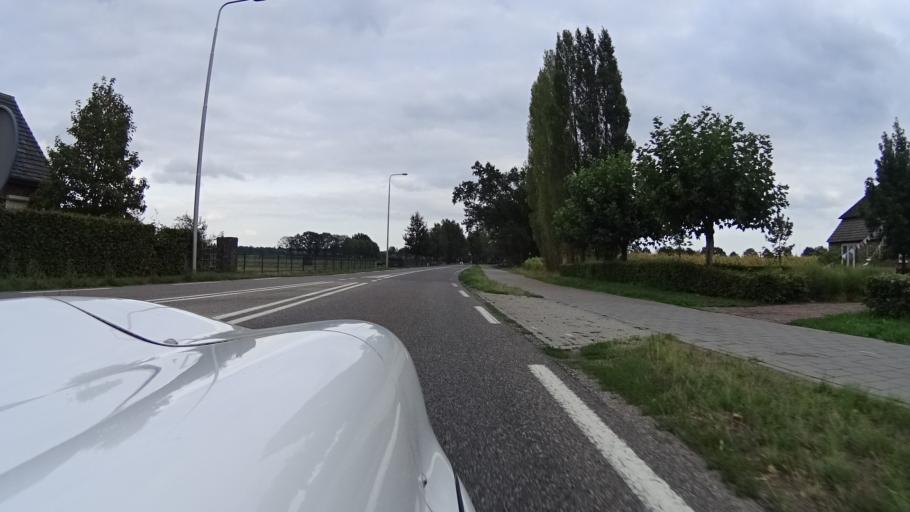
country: NL
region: North Brabant
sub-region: Gemeente Boekel
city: Boekel
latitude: 51.5849
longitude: 5.6844
